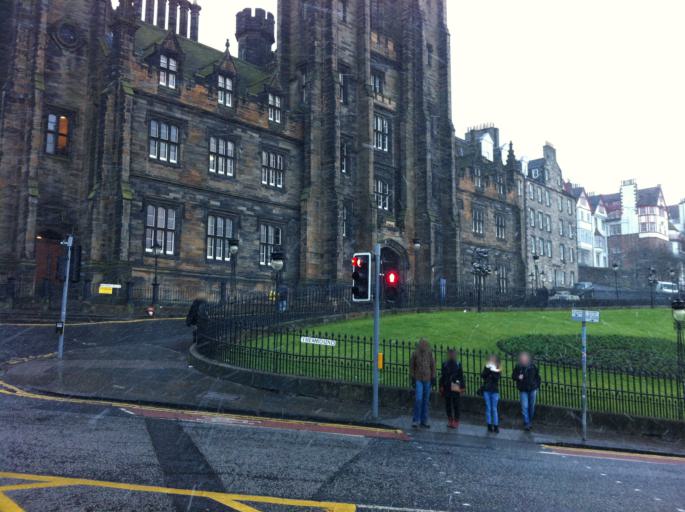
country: GB
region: Scotland
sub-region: Edinburgh
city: Edinburgh
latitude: 55.9502
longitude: -3.1948
